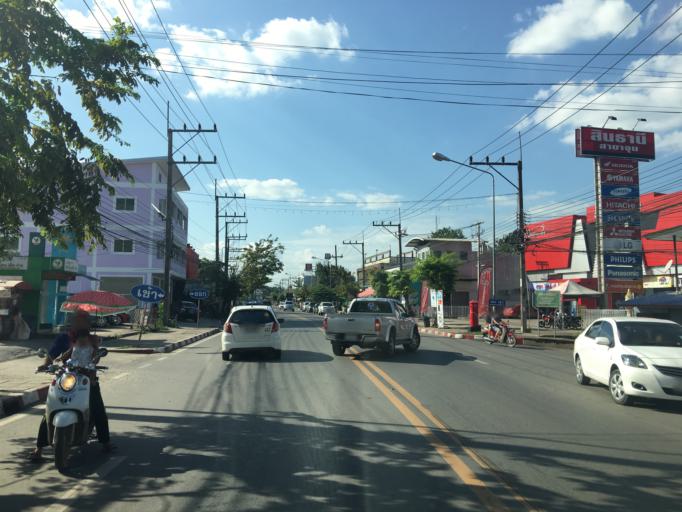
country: TH
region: Phayao
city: Chun
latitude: 19.3408
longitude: 100.1247
